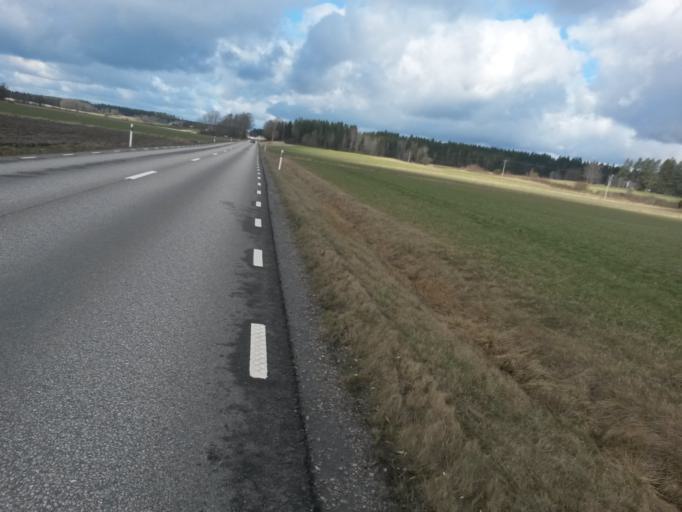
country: SE
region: Vaestra Goetaland
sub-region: Vargarda Kommun
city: Vargarda
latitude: 58.0483
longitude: 12.7818
